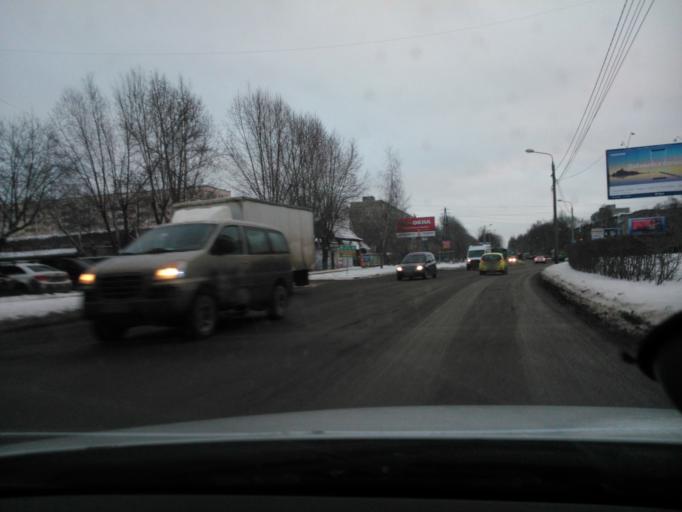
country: RU
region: Perm
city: Kondratovo
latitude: 57.9671
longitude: 56.1751
